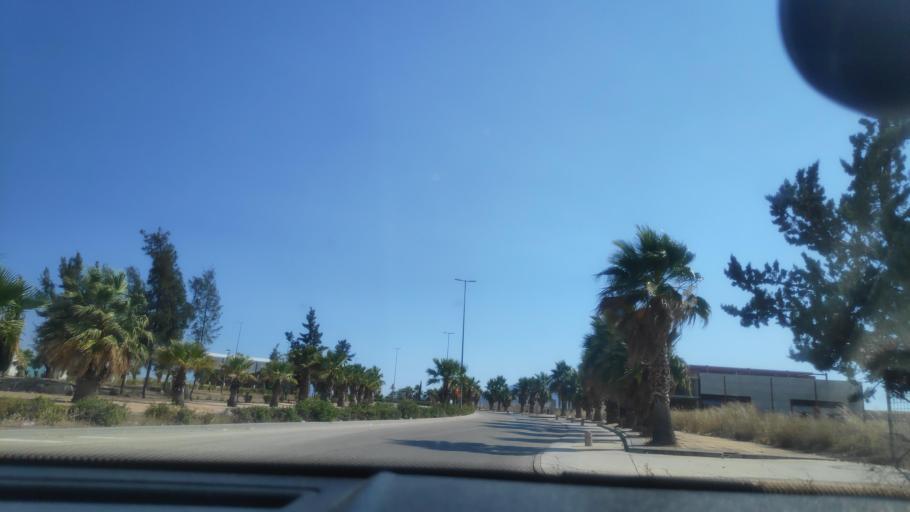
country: ES
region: Andalusia
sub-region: Provincia de Jaen
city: Jaen
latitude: 37.8270
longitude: -3.7759
